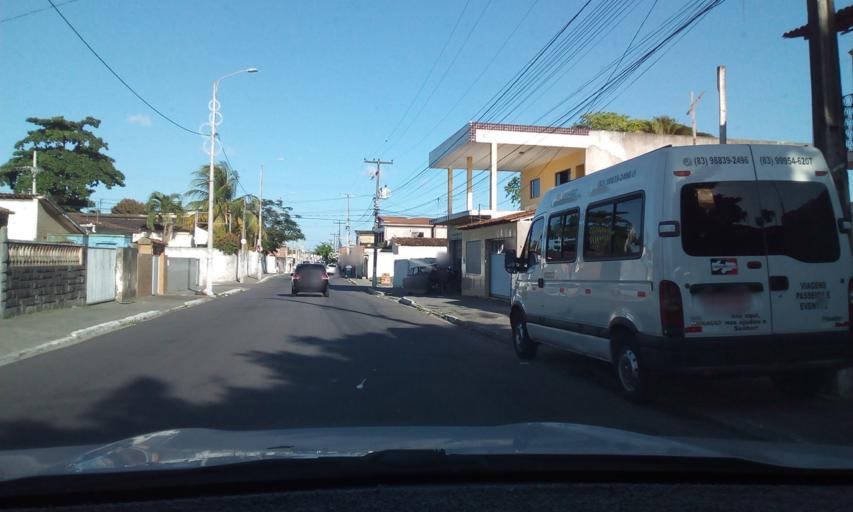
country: BR
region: Paraiba
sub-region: Bayeux
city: Bayeux
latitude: -7.1252
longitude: -34.9182
